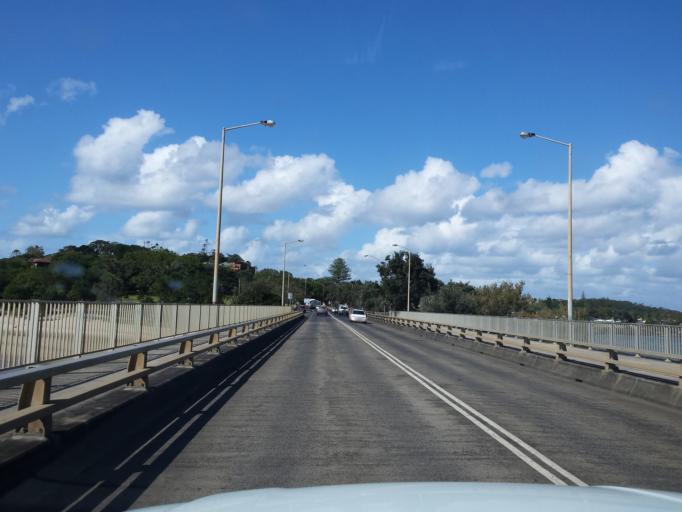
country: AU
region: New South Wales
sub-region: Ballina
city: East Ballina
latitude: -28.8684
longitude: 153.5766
